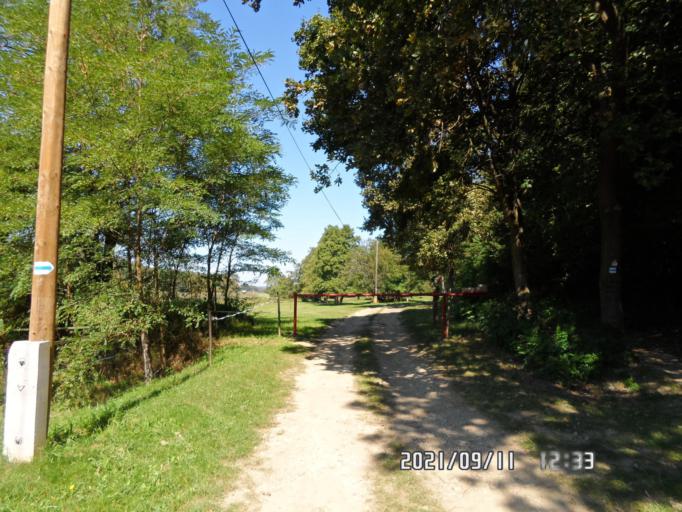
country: HU
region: Zala
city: Zalalovo
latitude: 46.7530
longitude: 16.7040
